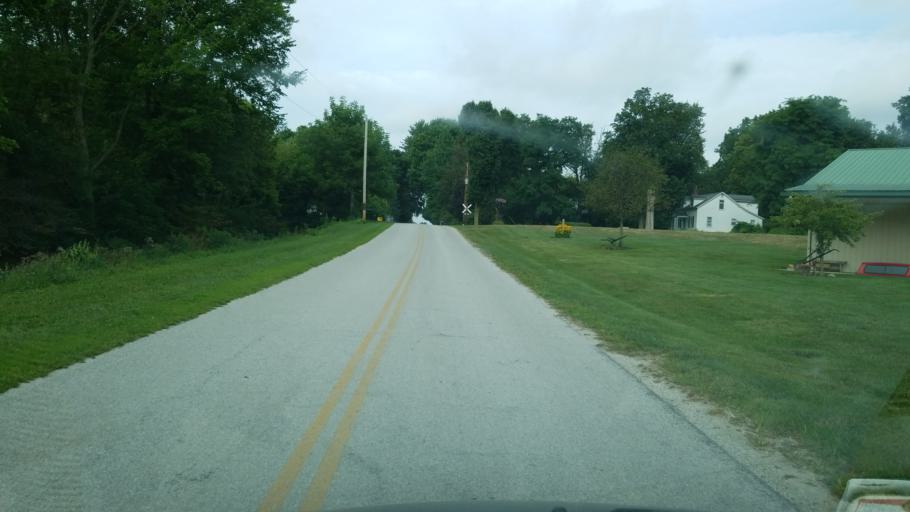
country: US
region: Ohio
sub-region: Sandusky County
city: Green Springs
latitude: 41.1896
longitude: -83.1055
